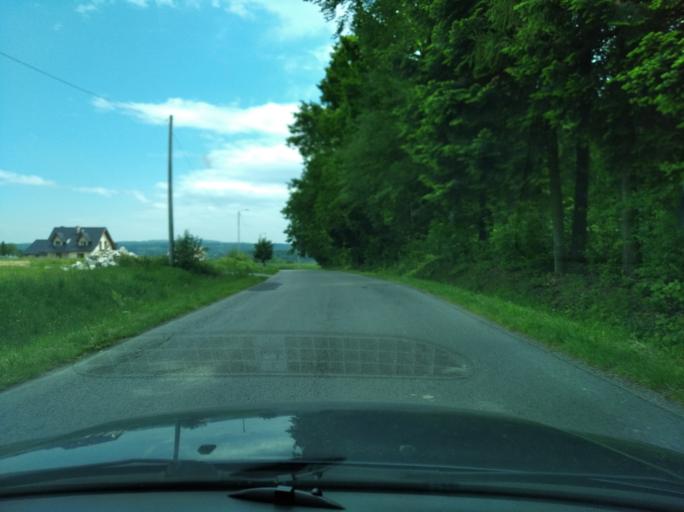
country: PL
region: Subcarpathian Voivodeship
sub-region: Powiat ropczycko-sedziszowski
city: Ropczyce
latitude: 50.0082
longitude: 21.6126
